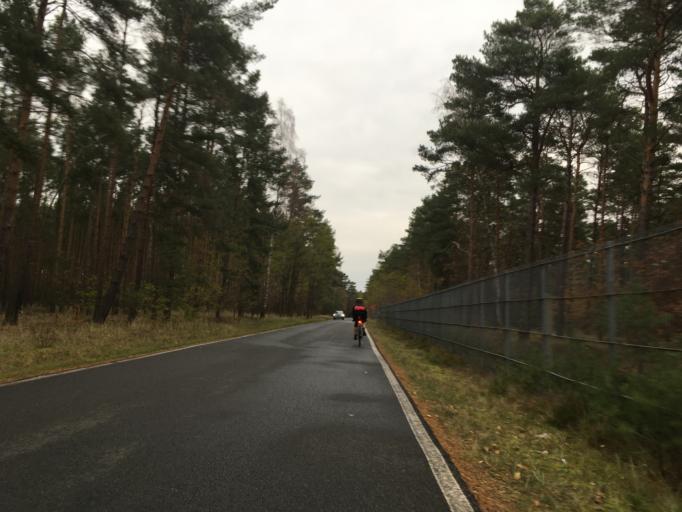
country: DE
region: Brandenburg
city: Mullrose
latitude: 52.2716
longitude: 14.4794
